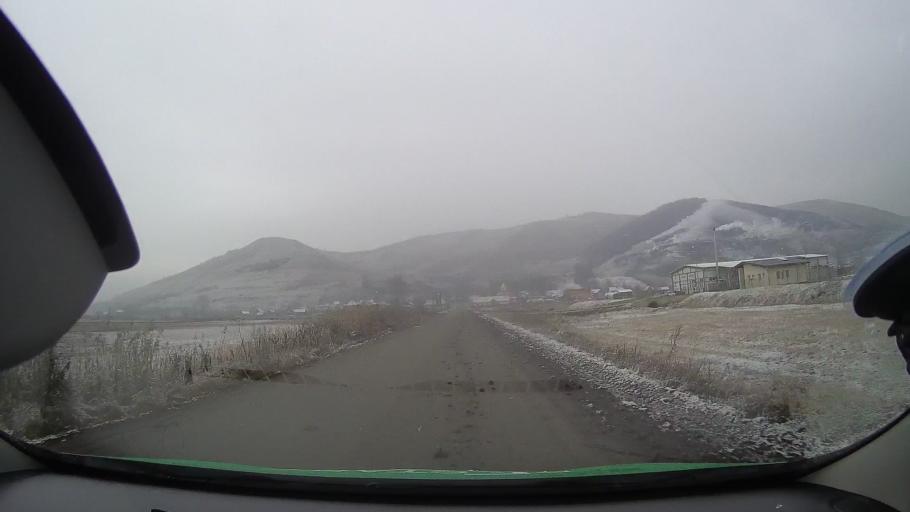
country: RO
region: Alba
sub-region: Comuna Noslac
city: Noslac
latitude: 46.3469
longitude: 23.9327
